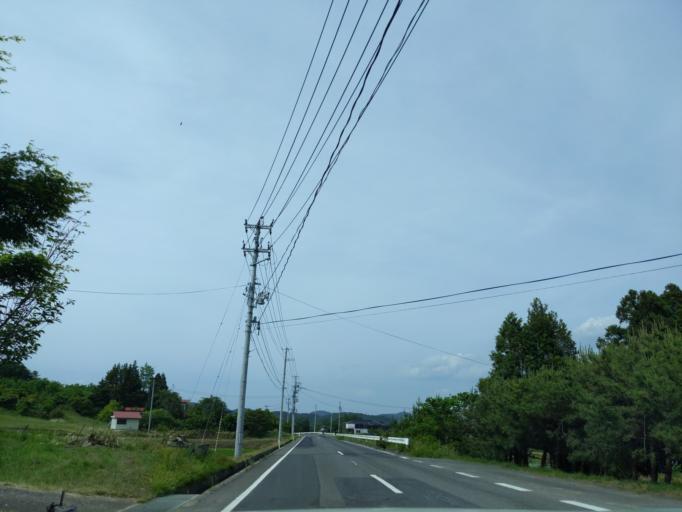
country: JP
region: Fukushima
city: Koriyama
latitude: 37.4616
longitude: 140.3128
